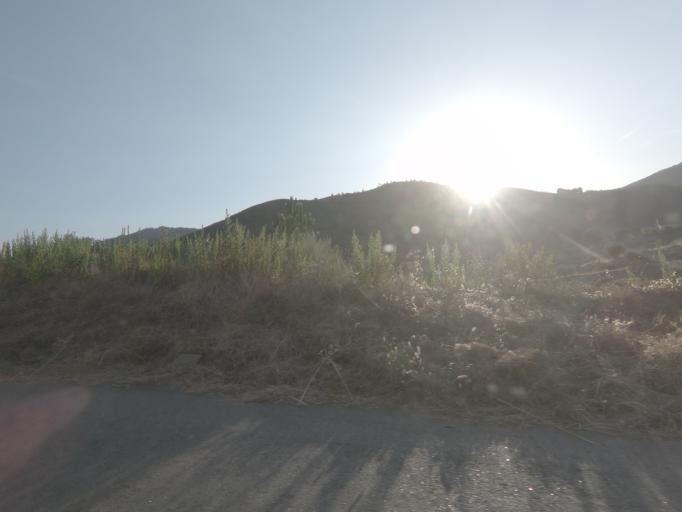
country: PT
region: Vila Real
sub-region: Sabrosa
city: Vilela
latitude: 41.1917
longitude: -7.6382
